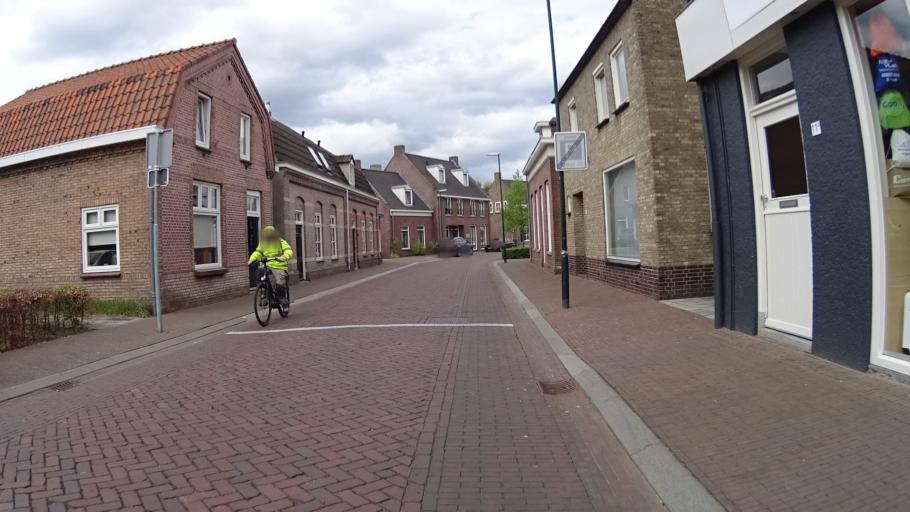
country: NL
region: North Brabant
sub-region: Gemeente Boekel
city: Boekel
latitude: 51.5584
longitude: 5.6827
